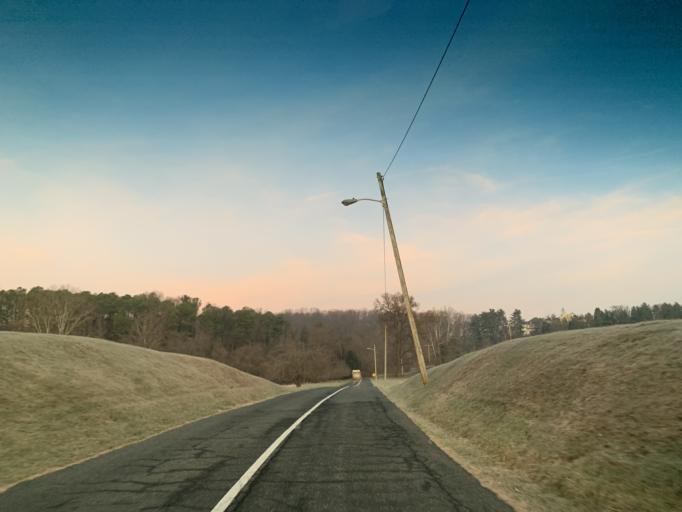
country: US
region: Maryland
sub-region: Baltimore County
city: Carney
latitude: 39.4430
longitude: -76.5150
